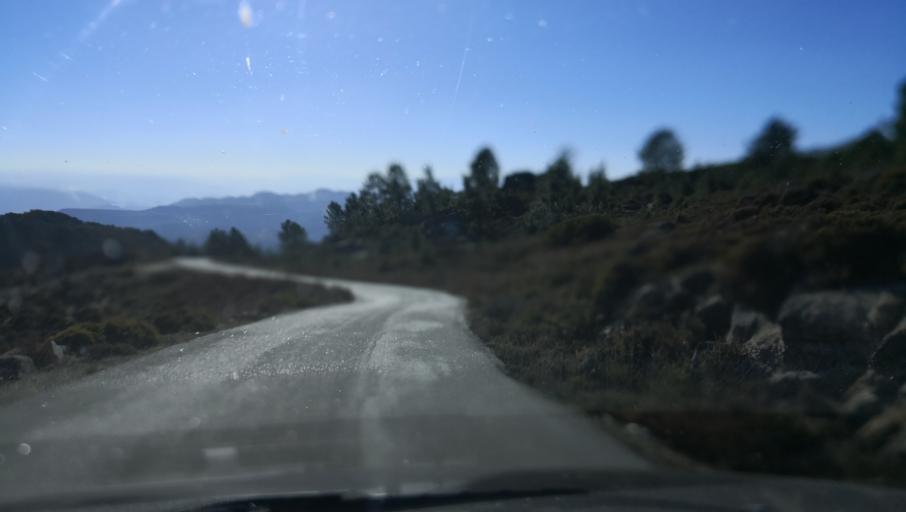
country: PT
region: Vila Real
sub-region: Vila Real
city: Vila Real
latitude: 41.3273
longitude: -7.7898
